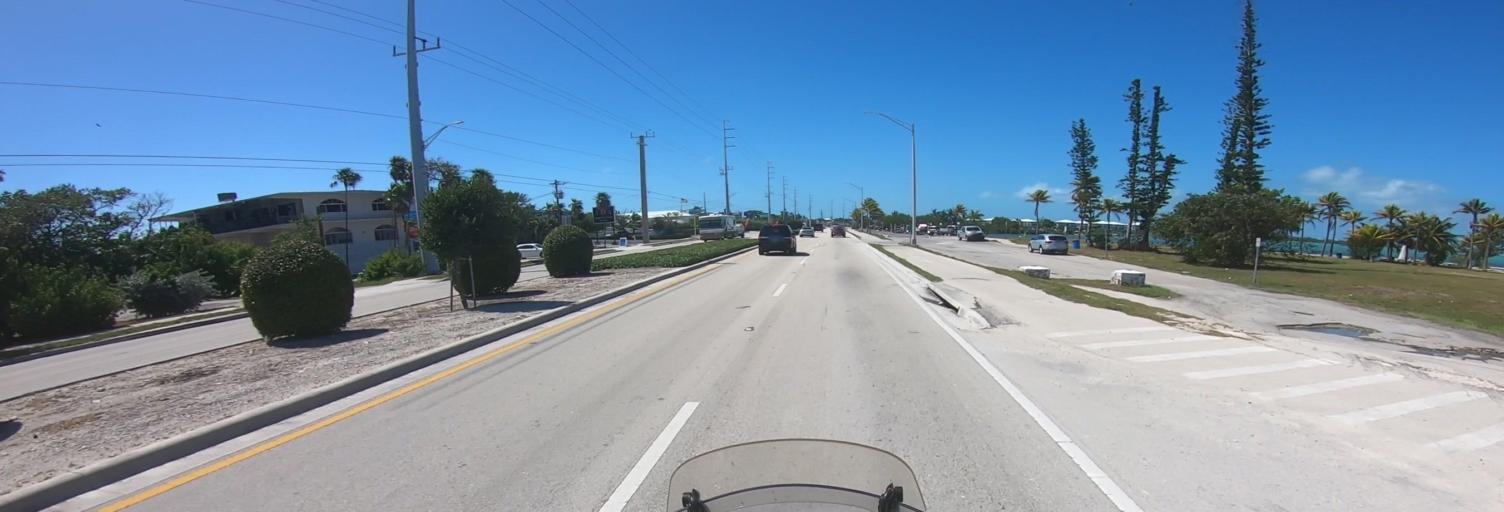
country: US
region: Florida
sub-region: Monroe County
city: Marathon
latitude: 24.7342
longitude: -81.0163
